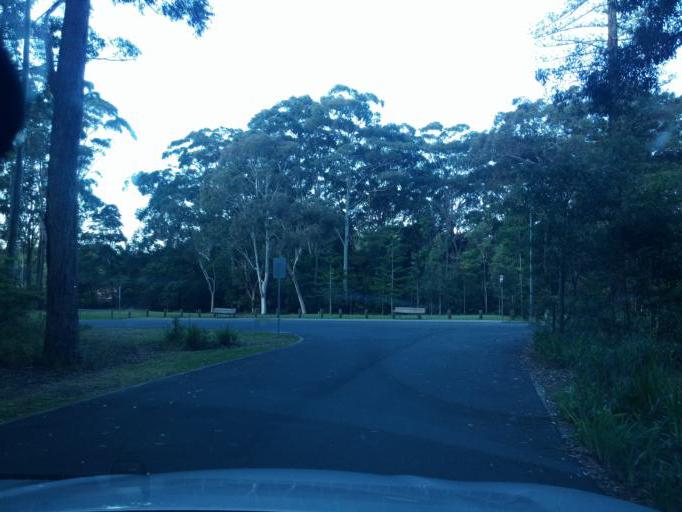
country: AU
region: New South Wales
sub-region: Port Macquarie-Hastings
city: Port Macquarie
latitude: -31.4420
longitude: 152.9188
